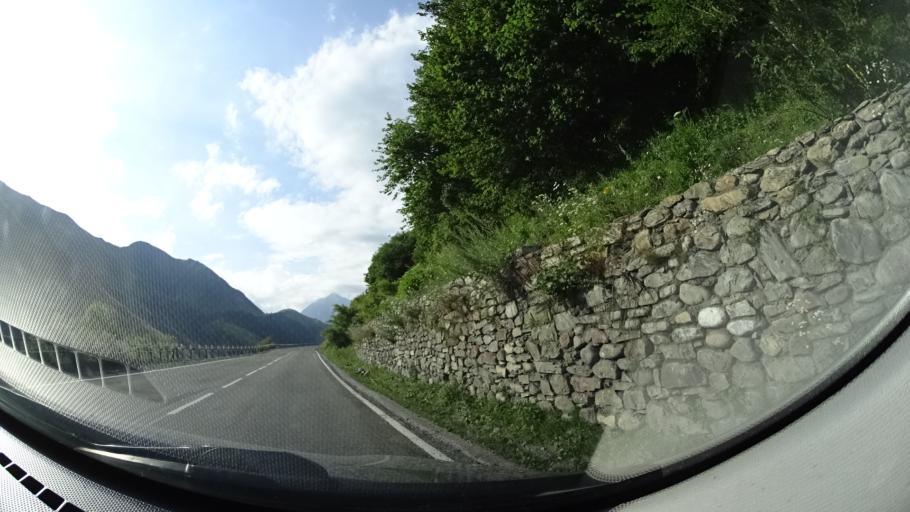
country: GE
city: Gudauri
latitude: 42.4412
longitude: 44.4835
